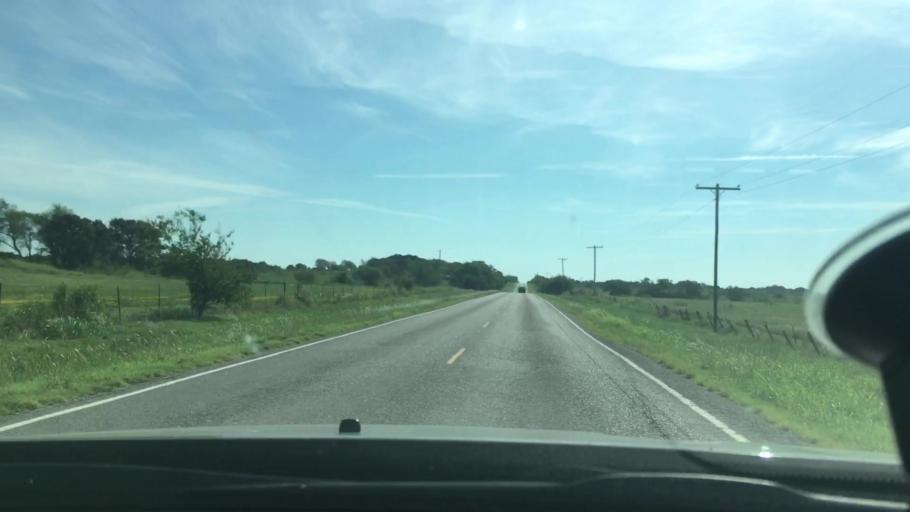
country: US
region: Oklahoma
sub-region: Carter County
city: Ardmore
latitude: 34.3327
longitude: -97.2001
